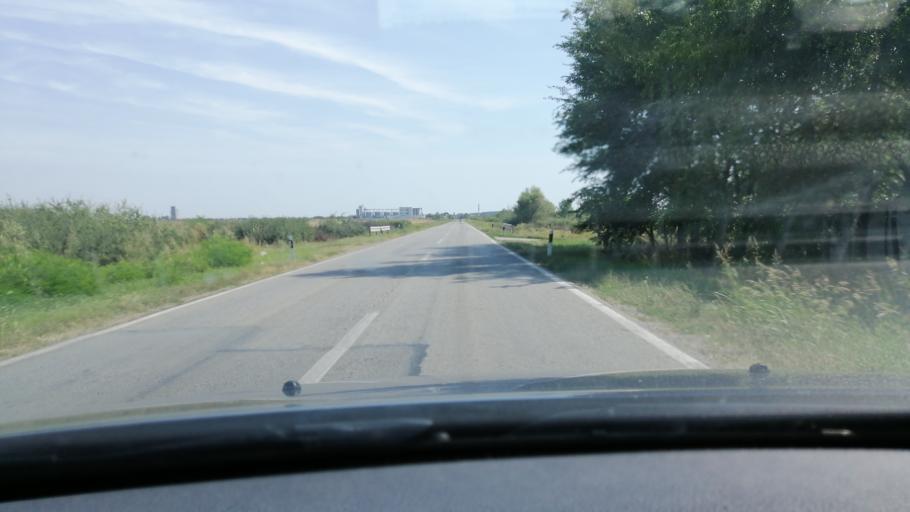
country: RS
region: Autonomna Pokrajina Vojvodina
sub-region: Srednjebanatski Okrug
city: Secanj
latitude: 45.3741
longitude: 20.7419
